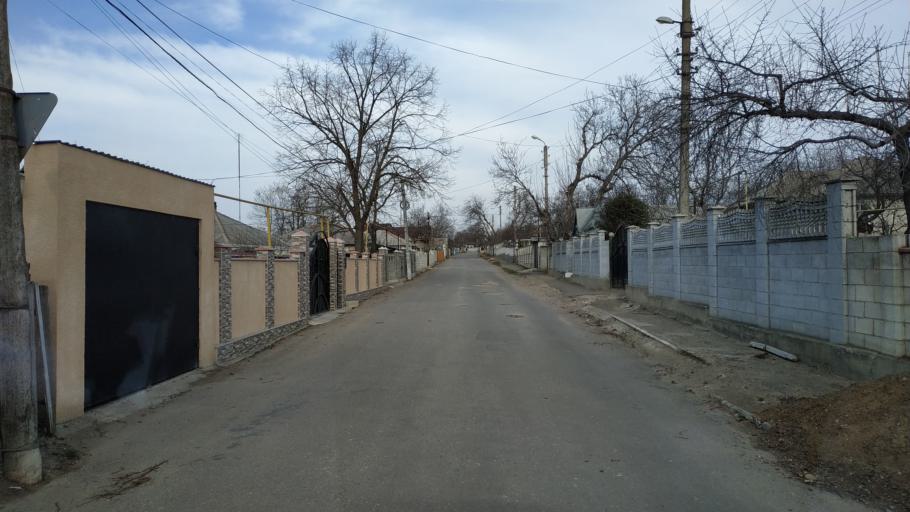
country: MD
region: Chisinau
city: Vatra
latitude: 46.9840
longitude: 28.6726
